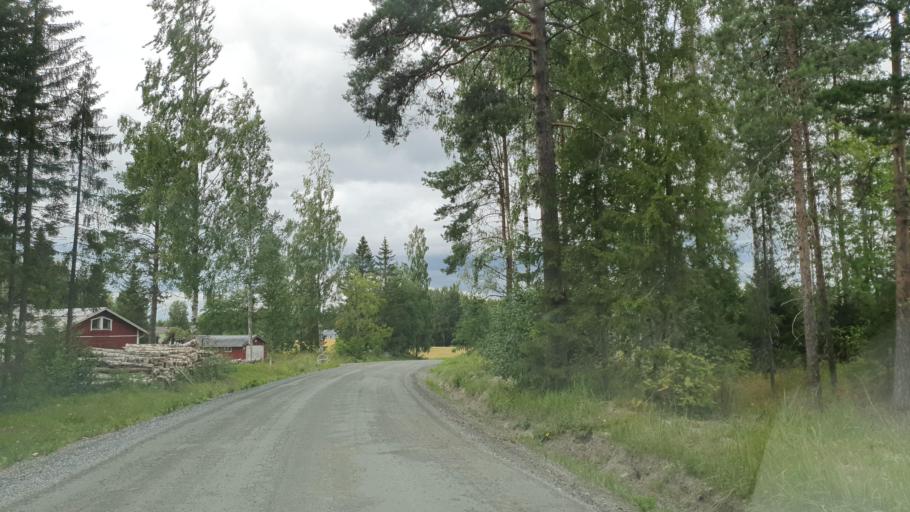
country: FI
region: Northern Savo
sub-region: Ylae-Savo
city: Iisalmi
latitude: 63.5185
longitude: 27.1016
